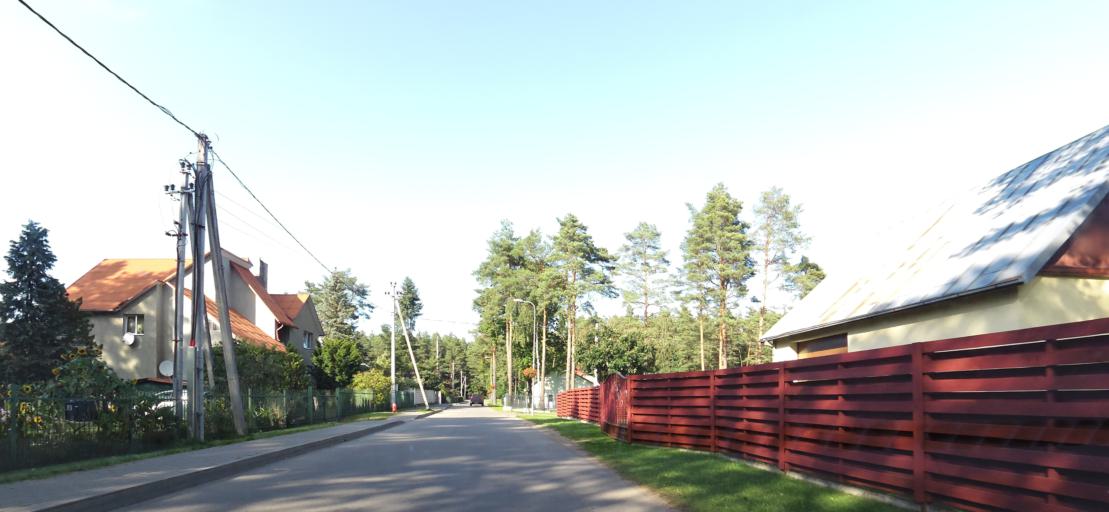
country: LT
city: Baltoji Voke
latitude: 54.5834
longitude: 25.2606
